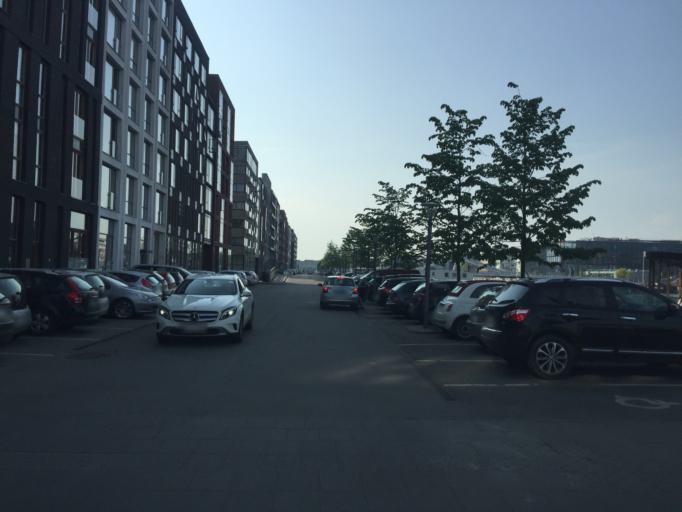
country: DK
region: Capital Region
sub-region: Kobenhavn
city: Copenhagen
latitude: 55.6463
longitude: 12.5529
